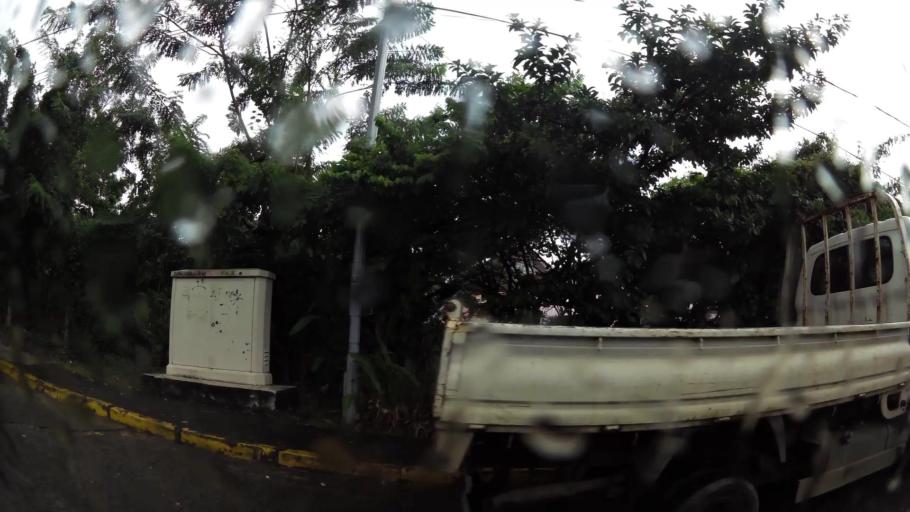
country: MQ
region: Martinique
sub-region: Martinique
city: Les Trois-Ilets
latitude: 14.5403
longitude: -61.0379
